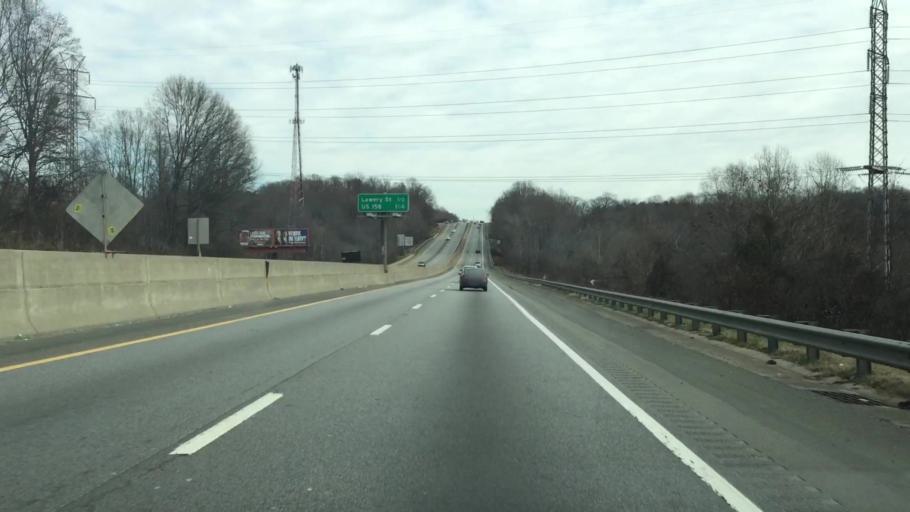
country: US
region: North Carolina
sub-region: Forsyth County
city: Winston-Salem
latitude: 36.0946
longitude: -80.2196
